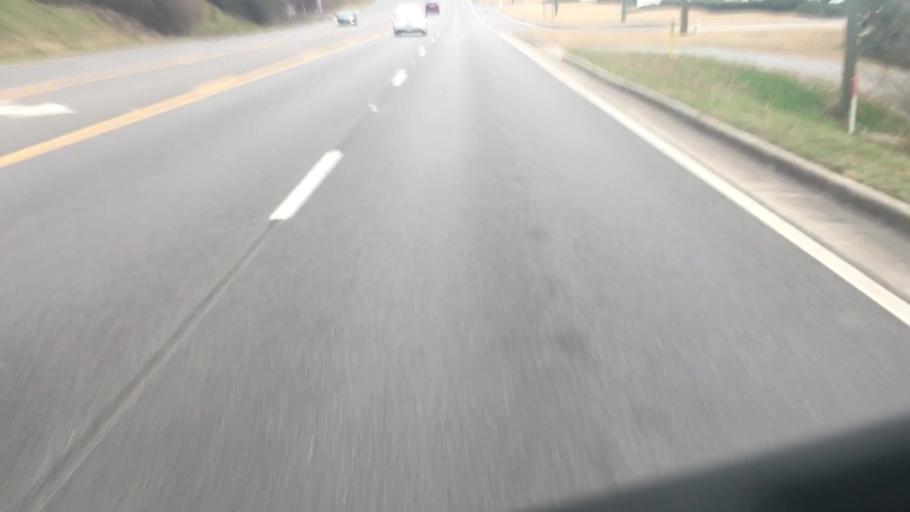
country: US
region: Alabama
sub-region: Jefferson County
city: Hoover
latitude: 33.3586
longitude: -86.8340
